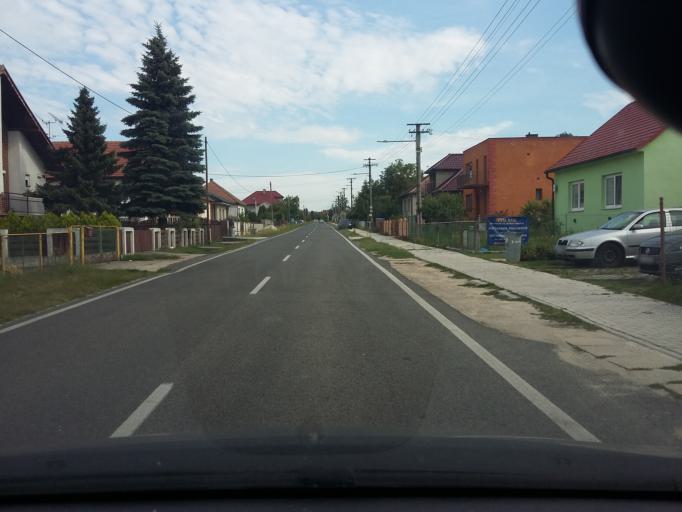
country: SK
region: Trnavsky
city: Gbely
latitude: 48.6367
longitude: 17.2009
